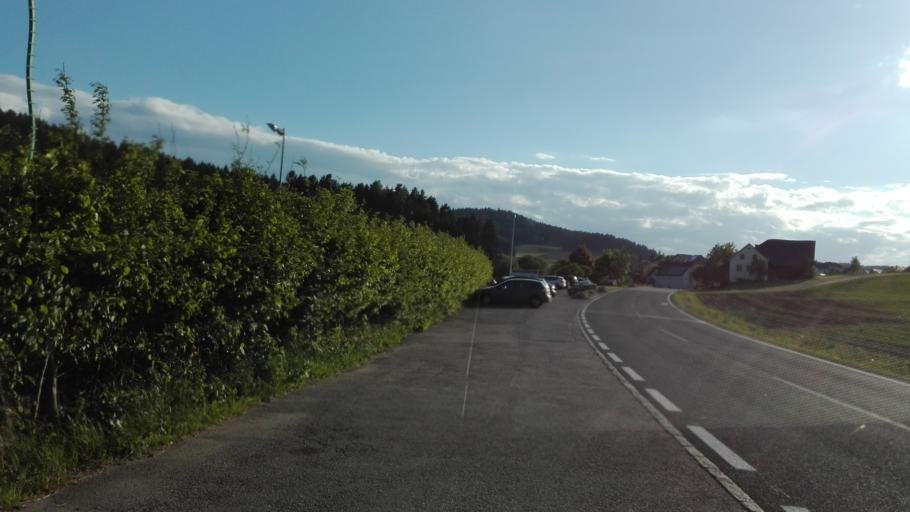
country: AT
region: Upper Austria
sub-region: Politischer Bezirk Freistadt
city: Freistadt
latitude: 48.4152
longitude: 14.6036
